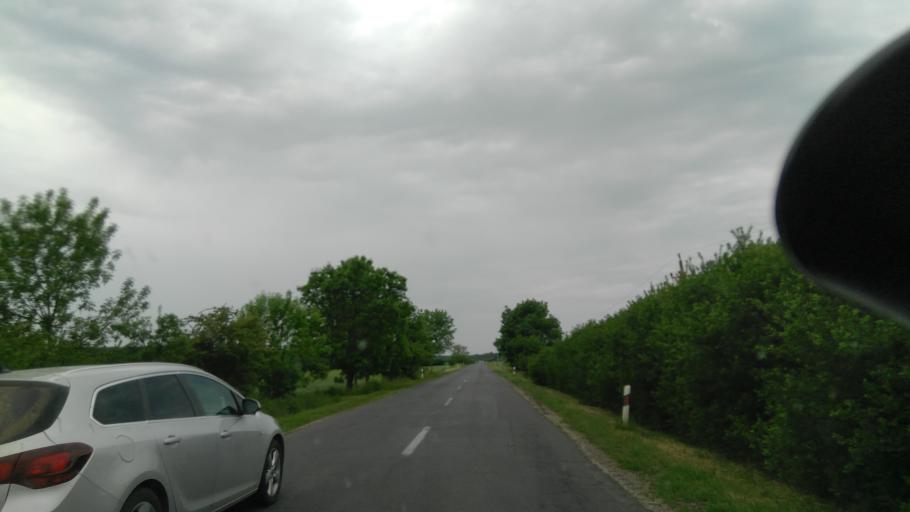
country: HU
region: Bekes
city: Doboz
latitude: 46.7258
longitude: 21.2914
